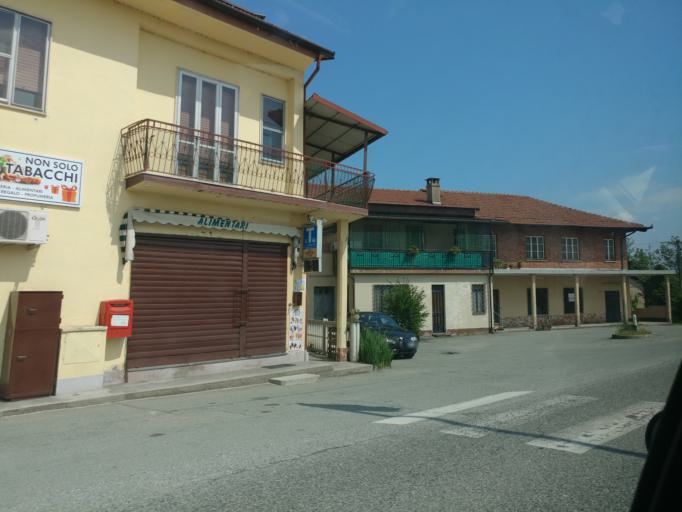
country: IT
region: Piedmont
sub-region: Provincia di Torino
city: Cavour
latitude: 44.7484
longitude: 7.4084
